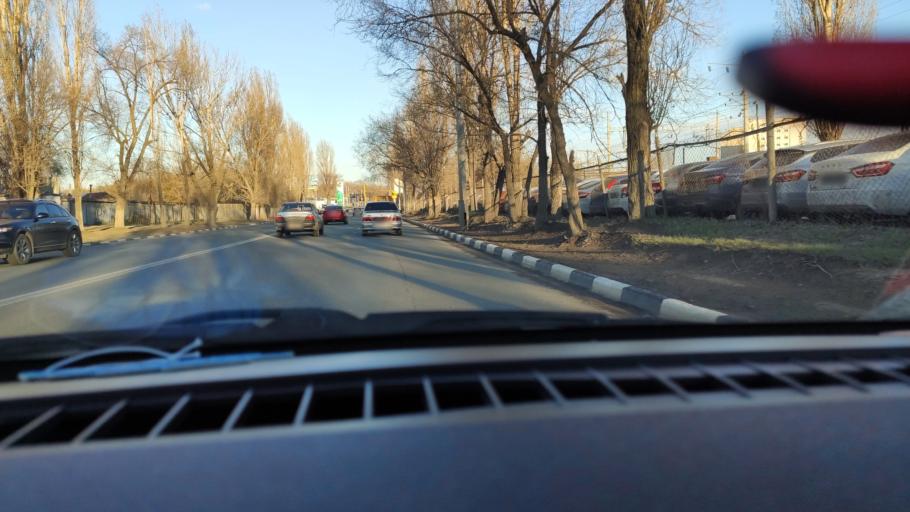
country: RU
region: Saratov
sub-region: Saratovskiy Rayon
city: Saratov
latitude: 51.5791
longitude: 45.9837
